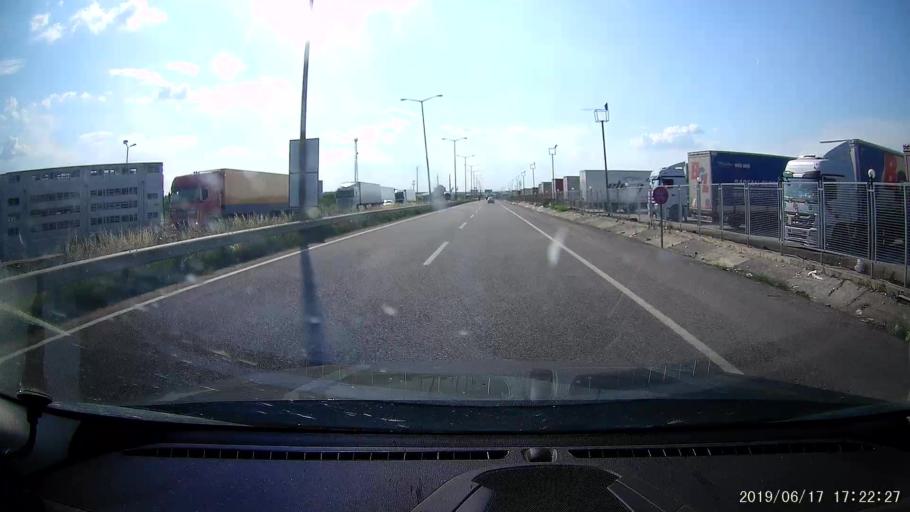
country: GR
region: East Macedonia and Thrace
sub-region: Nomos Evrou
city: Rizia
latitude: 41.7116
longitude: 26.3743
